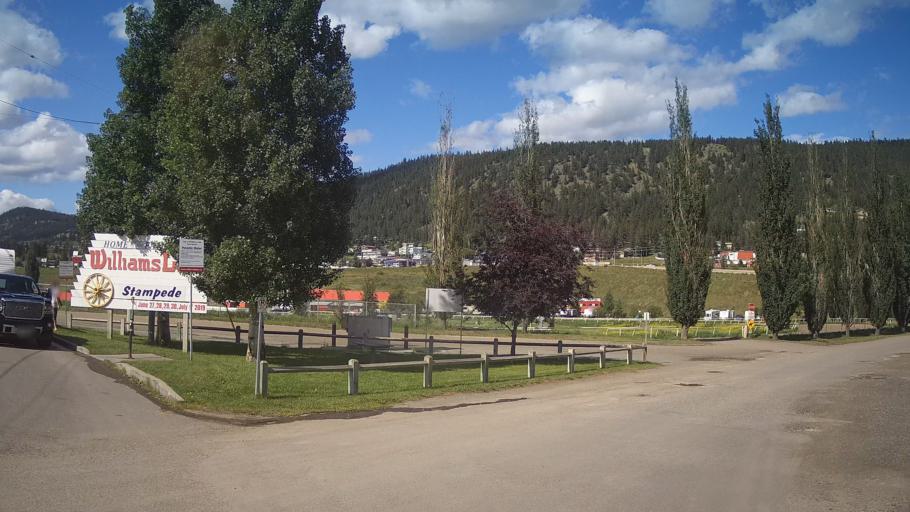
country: CA
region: British Columbia
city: Williams Lake
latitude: 52.1237
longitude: -122.1317
